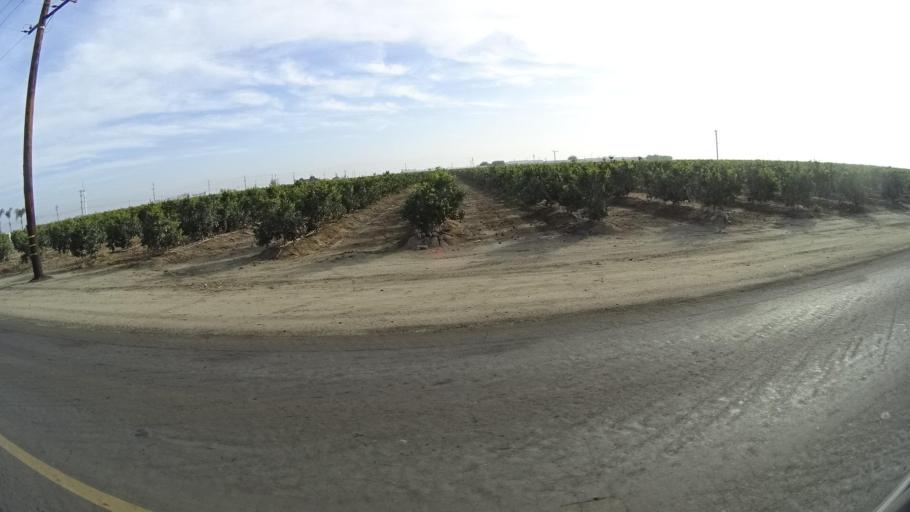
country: US
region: California
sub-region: Kern County
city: Delano
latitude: 35.7740
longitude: -119.2053
